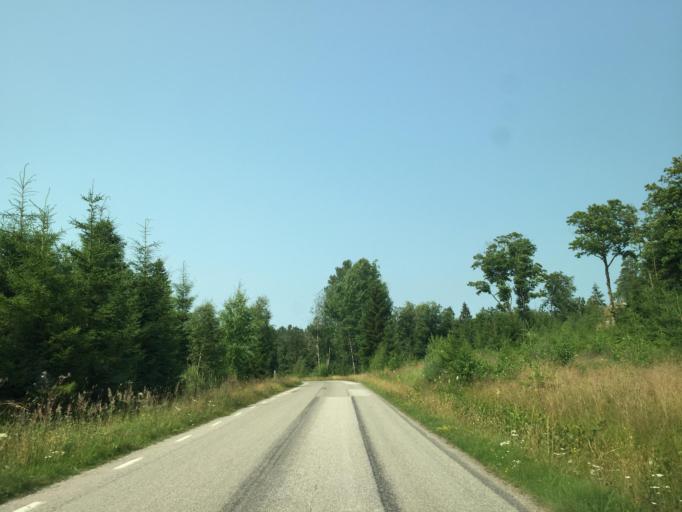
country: SE
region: Vaestra Goetaland
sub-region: Trollhattan
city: Sjuntorp
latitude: 58.3050
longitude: 12.1312
